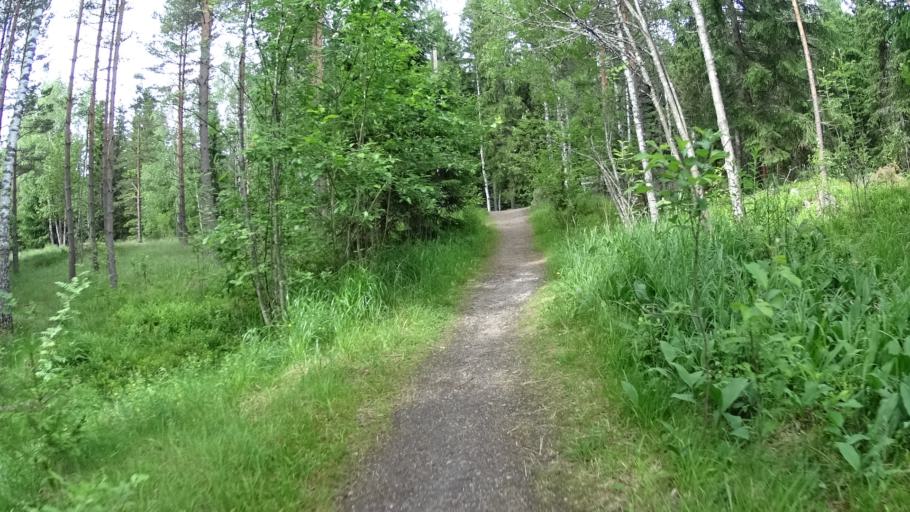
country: FI
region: Uusimaa
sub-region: Helsinki
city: Espoo
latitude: 60.2821
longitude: 24.5059
